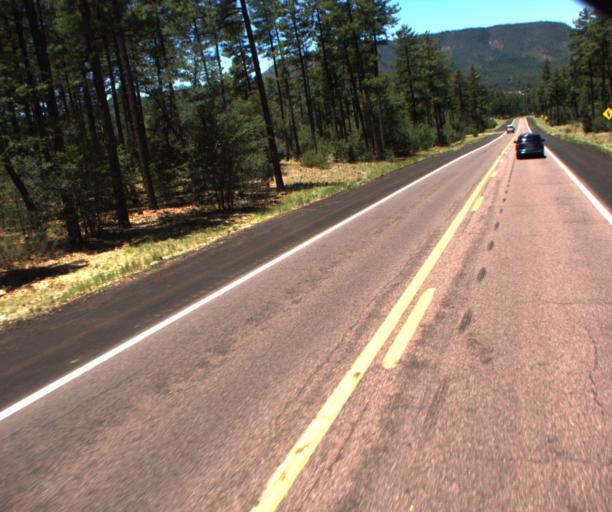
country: US
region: Arizona
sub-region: Gila County
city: Pine
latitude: 34.3682
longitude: -111.4373
